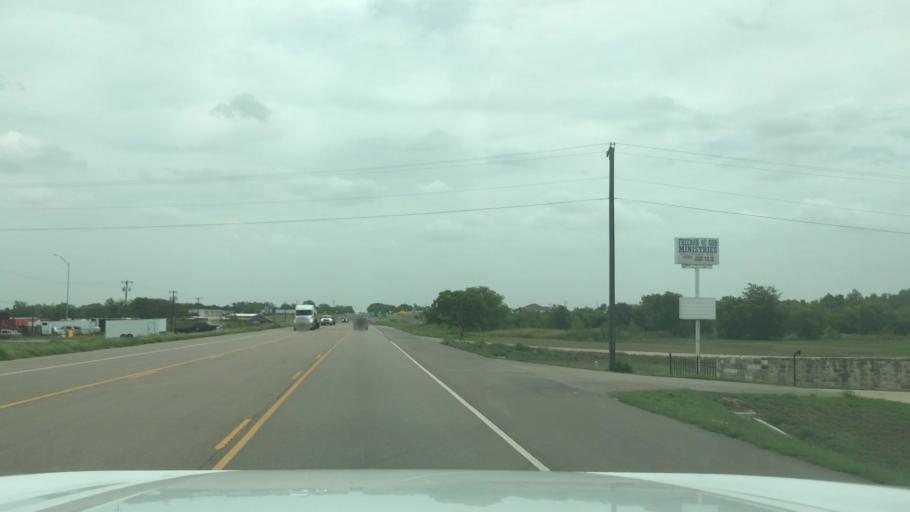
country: US
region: Texas
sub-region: McLennan County
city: Woodway
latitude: 31.5782
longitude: -97.2975
